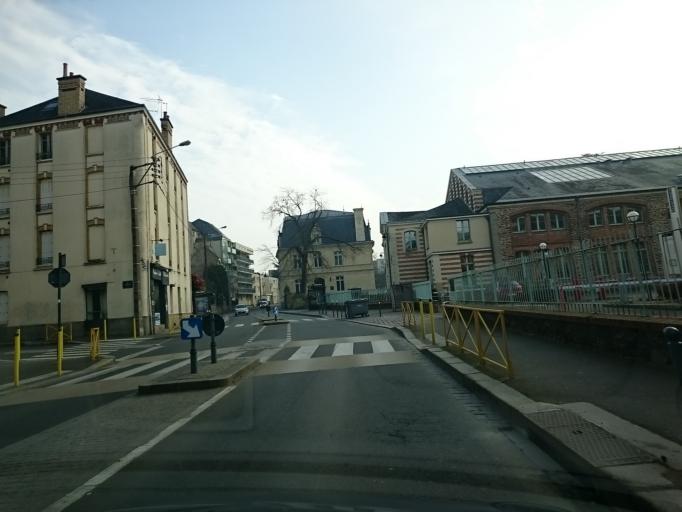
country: FR
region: Brittany
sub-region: Departement d'Ille-et-Vilaine
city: Rennes
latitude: 48.1132
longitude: -1.6619
